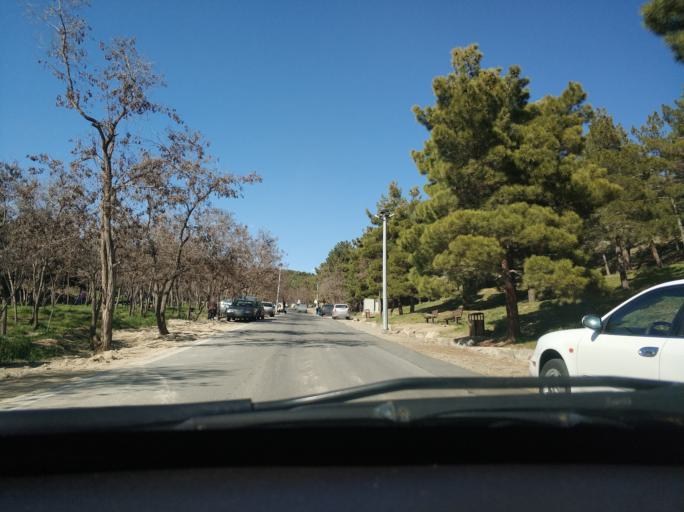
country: IR
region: Tehran
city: Tajrish
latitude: 35.7875
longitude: 51.5592
